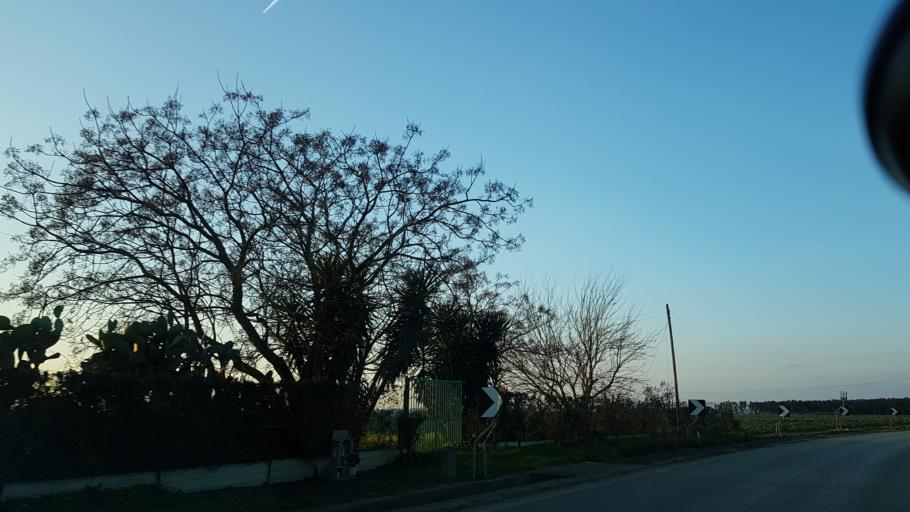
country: IT
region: Apulia
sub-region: Provincia di Brindisi
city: La Rosa
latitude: 40.6060
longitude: 17.9450
